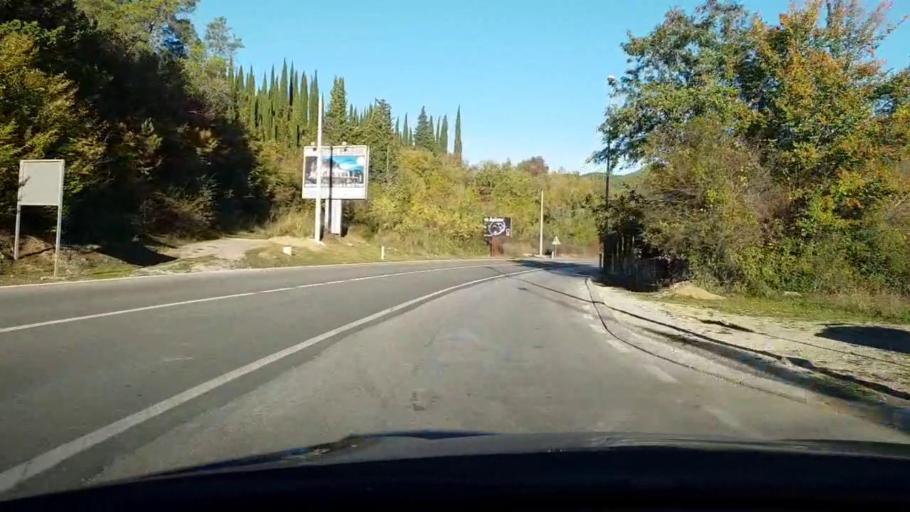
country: ME
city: Igalo
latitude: 42.4794
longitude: 18.4587
